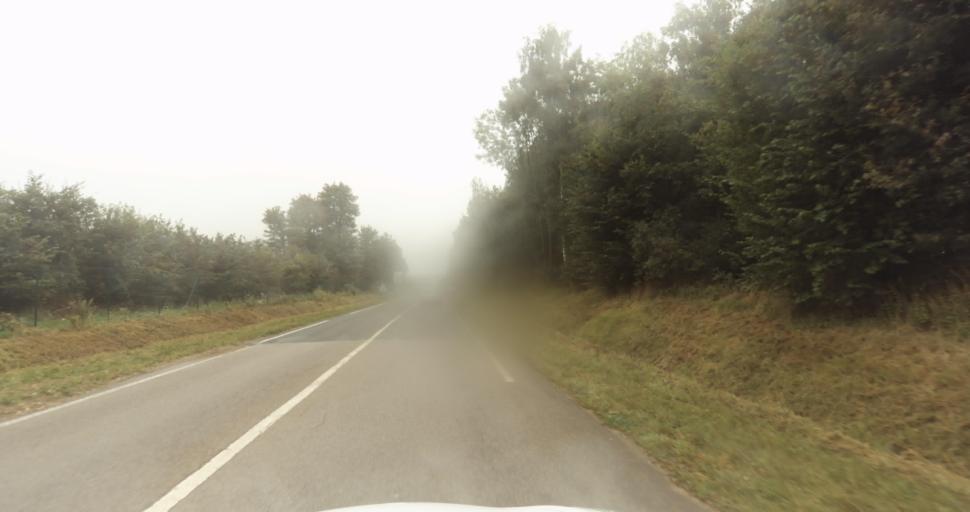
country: FR
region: Haute-Normandie
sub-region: Departement de l'Eure
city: Normanville
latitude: 49.0924
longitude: 1.1764
